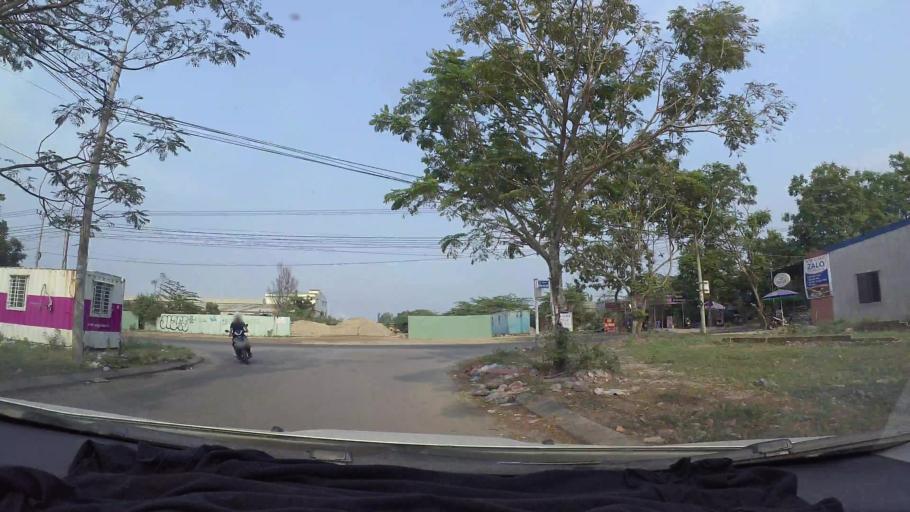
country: VN
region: Da Nang
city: Lien Chieu
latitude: 16.0508
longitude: 108.1599
